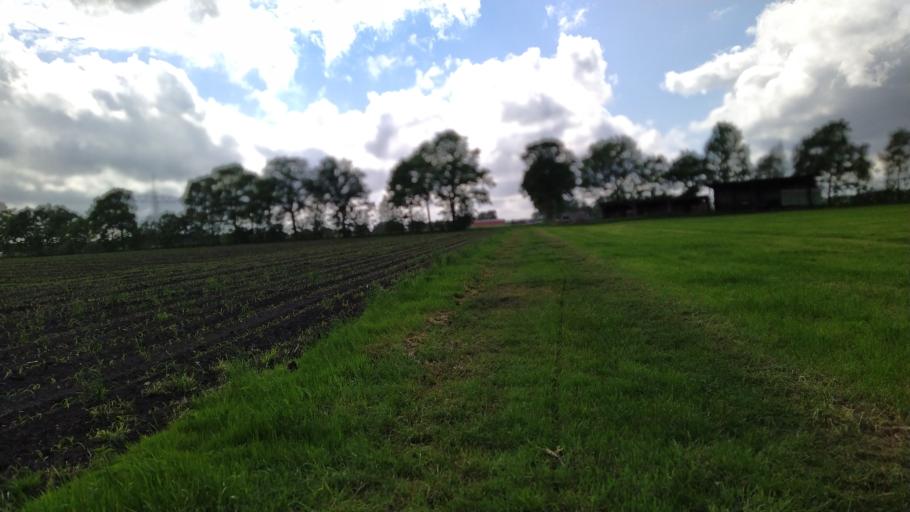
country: DE
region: Lower Saxony
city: Brest
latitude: 53.4572
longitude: 9.4084
